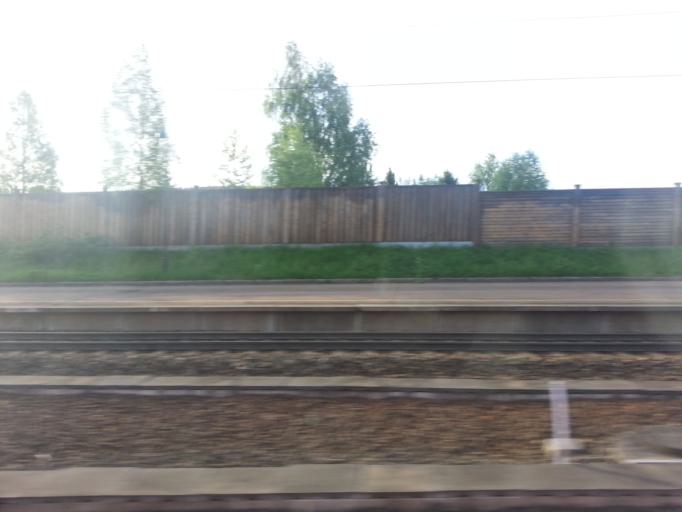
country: NO
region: Akershus
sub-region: Skedsmo
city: Leirsund
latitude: 60.0008
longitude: 11.0878
